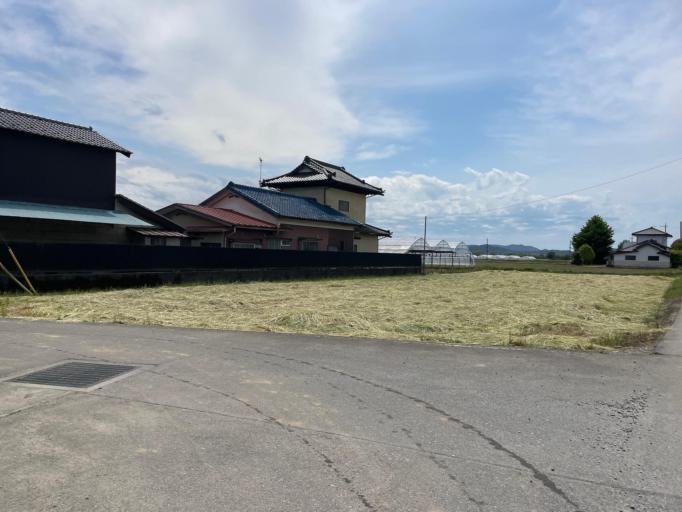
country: JP
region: Tochigi
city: Mibu
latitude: 36.4585
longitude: 139.7716
